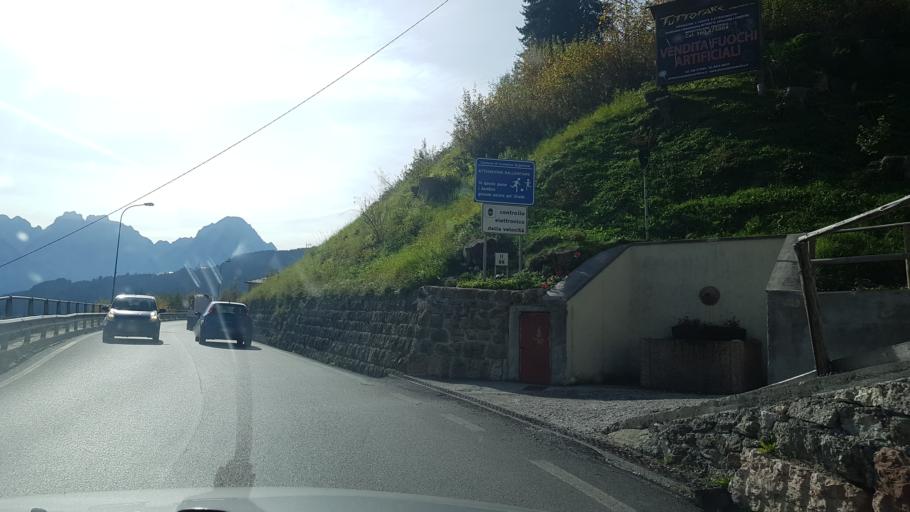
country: IT
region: Veneto
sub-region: Provincia di Belluno
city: Candide
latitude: 46.5927
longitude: 12.5192
